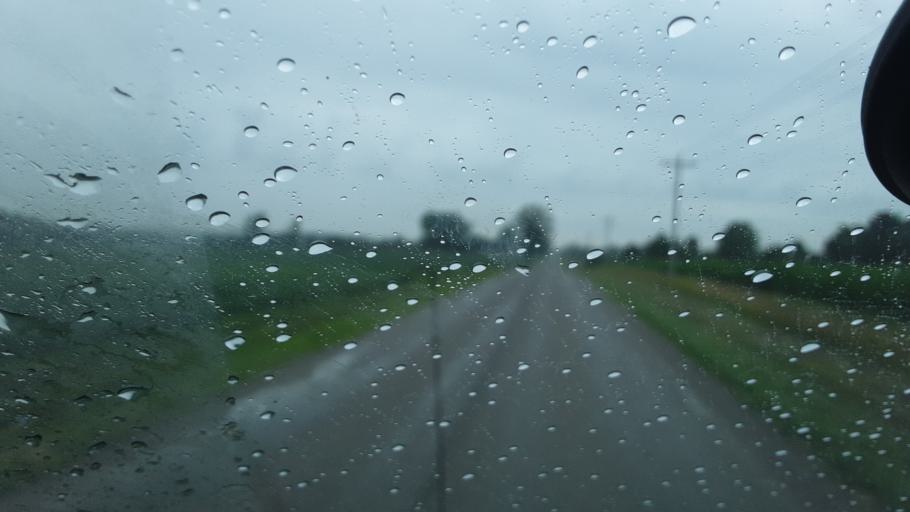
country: US
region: Ohio
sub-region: Williams County
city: Montpelier
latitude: 41.5948
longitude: -84.5743
